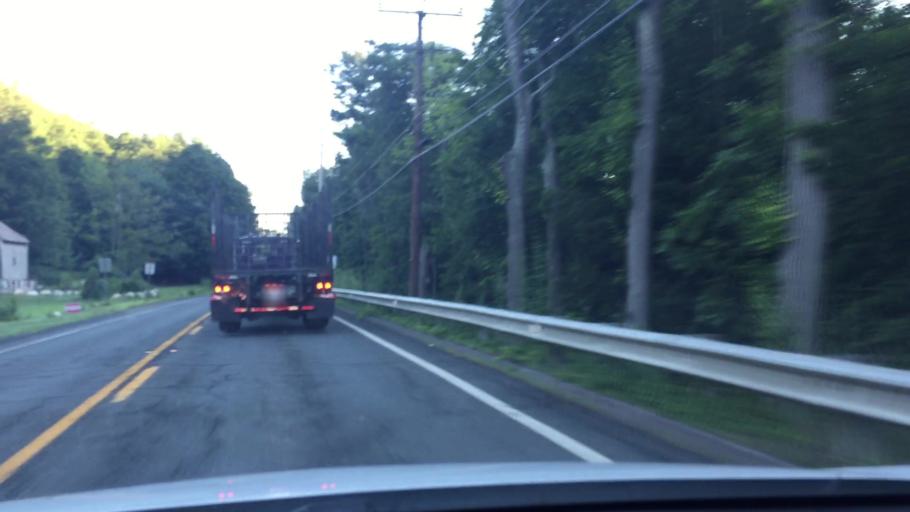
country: US
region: Massachusetts
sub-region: Hampshire County
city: Westhampton
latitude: 42.2082
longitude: -72.8553
